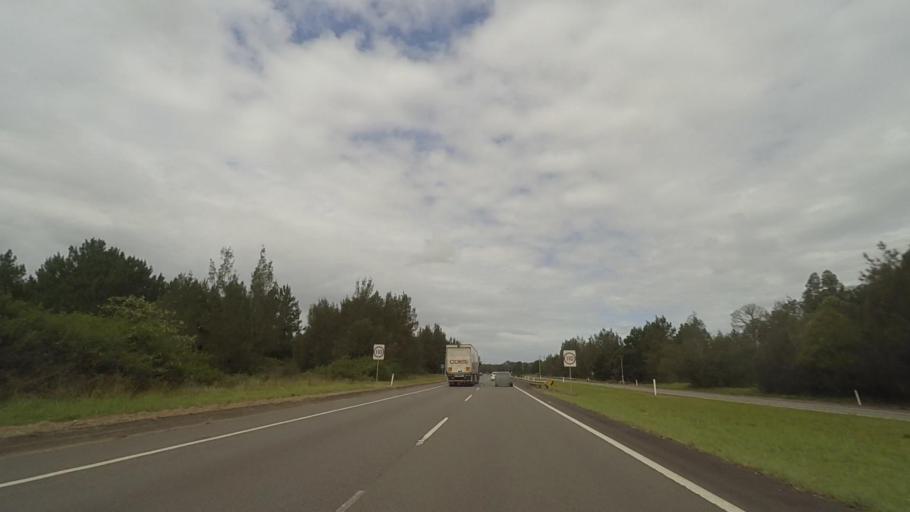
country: AU
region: New South Wales
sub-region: Port Stephens Shire
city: Raymond Terrace
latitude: -32.7793
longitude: 151.7476
